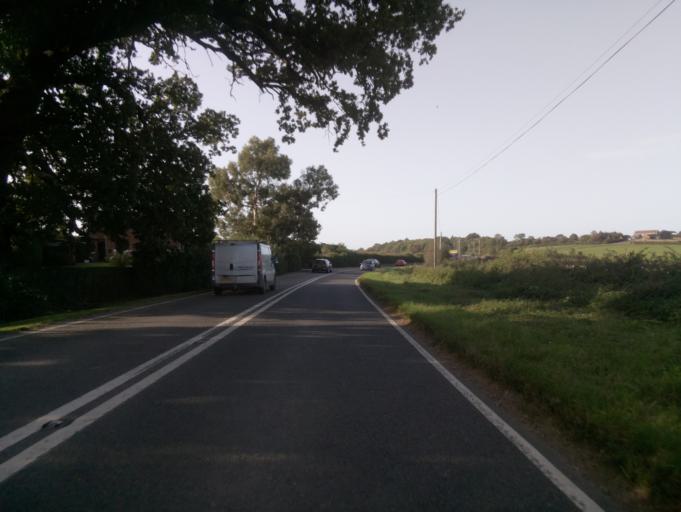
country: GB
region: England
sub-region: Gloucestershire
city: Gloucester
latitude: 51.9013
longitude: -2.2887
